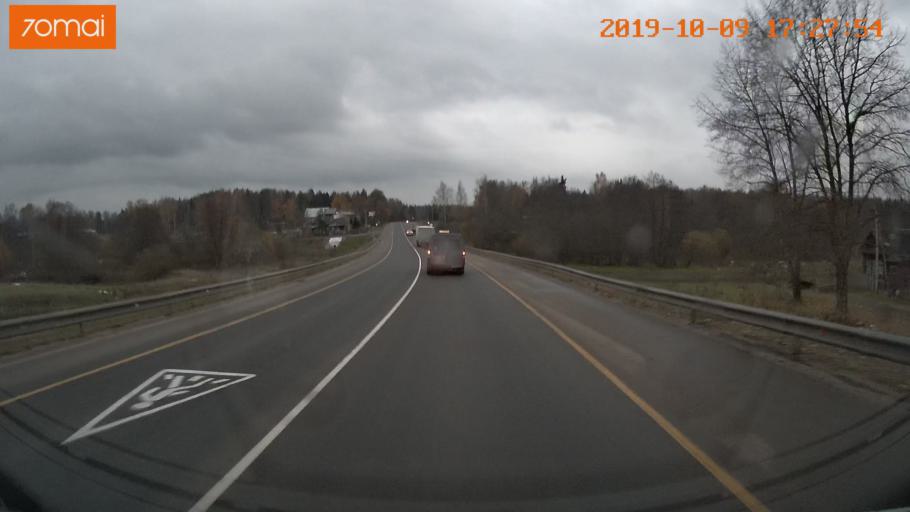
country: RU
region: Ivanovo
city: Furmanov
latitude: 57.1626
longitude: 41.0693
